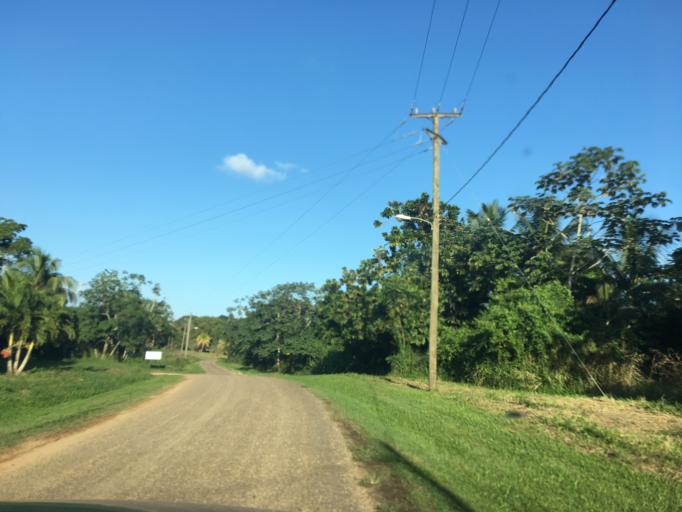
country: BZ
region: Stann Creek
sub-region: Dangriga
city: Dangriga
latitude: 16.8208
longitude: -88.3206
